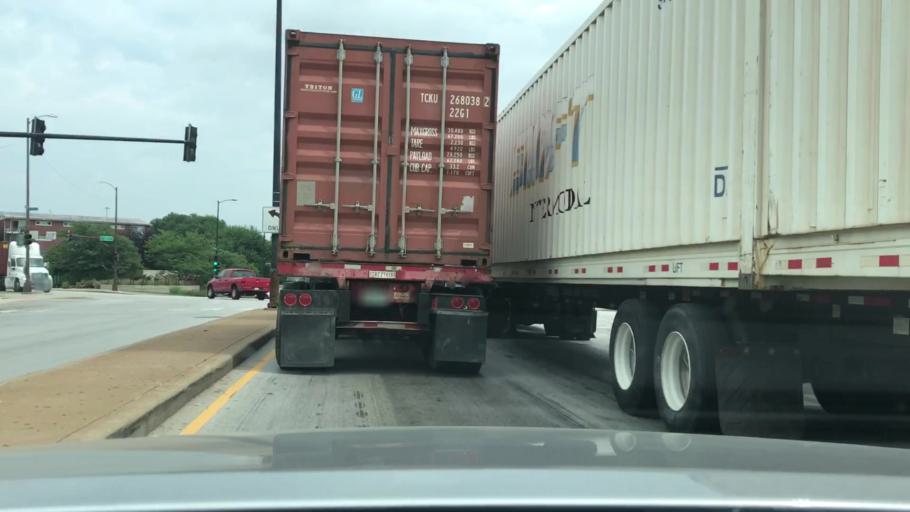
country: US
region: Illinois
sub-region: Cook County
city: Evergreen Park
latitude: 41.7498
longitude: -87.7041
